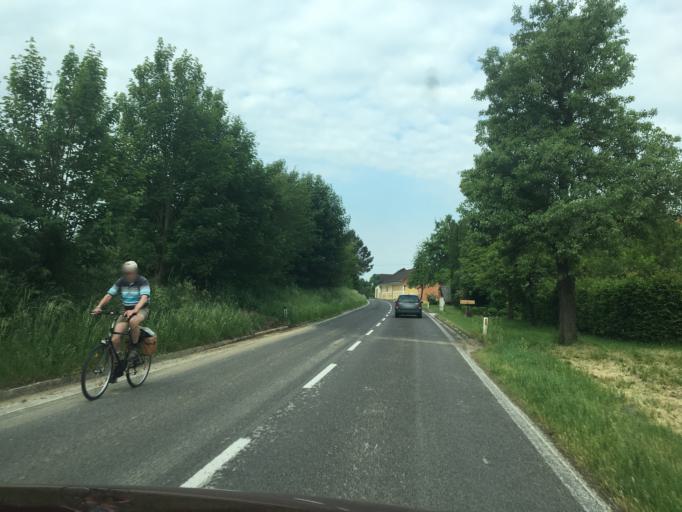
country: AT
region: Upper Austria
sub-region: Politischer Bezirk Grieskirchen
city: Grieskirchen
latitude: 48.2745
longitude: 13.7512
